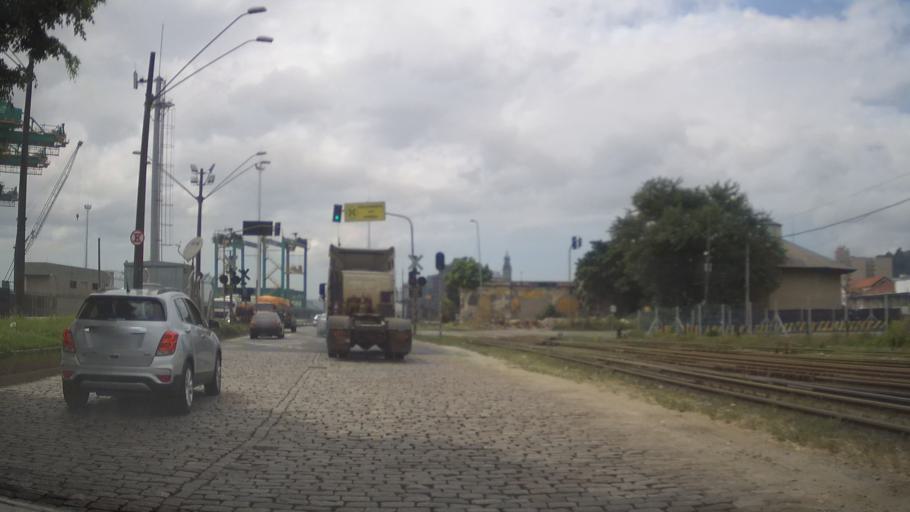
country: BR
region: Sao Paulo
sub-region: Santos
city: Santos
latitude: -23.9290
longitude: -46.3354
